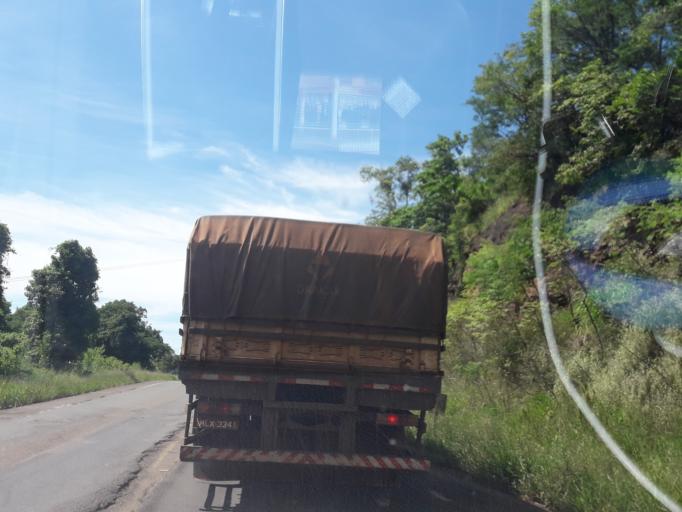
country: AR
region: Misiones
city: Bernardo de Irigoyen
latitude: -26.4888
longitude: -53.5044
